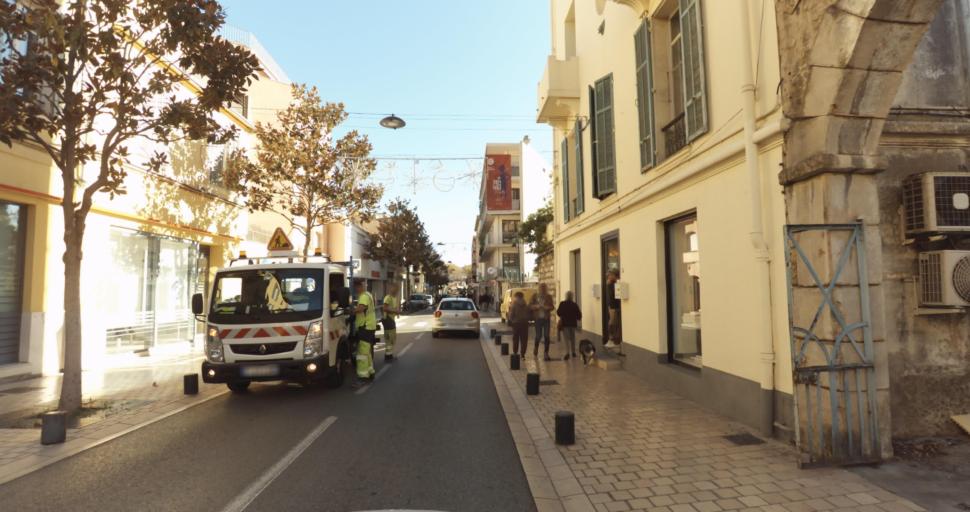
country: FR
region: Provence-Alpes-Cote d'Azur
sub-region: Departement des Alpes-Maritimes
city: Vence
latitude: 43.7229
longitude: 7.1095
